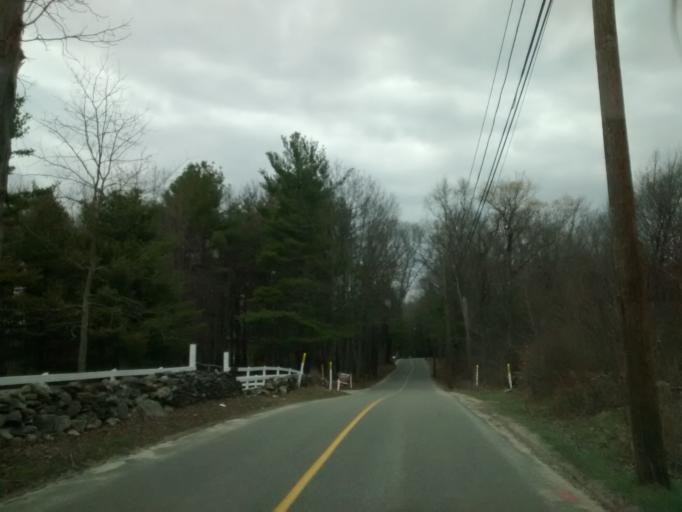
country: US
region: Massachusetts
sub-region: Worcester County
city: Southbridge
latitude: 42.1160
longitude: -72.0212
